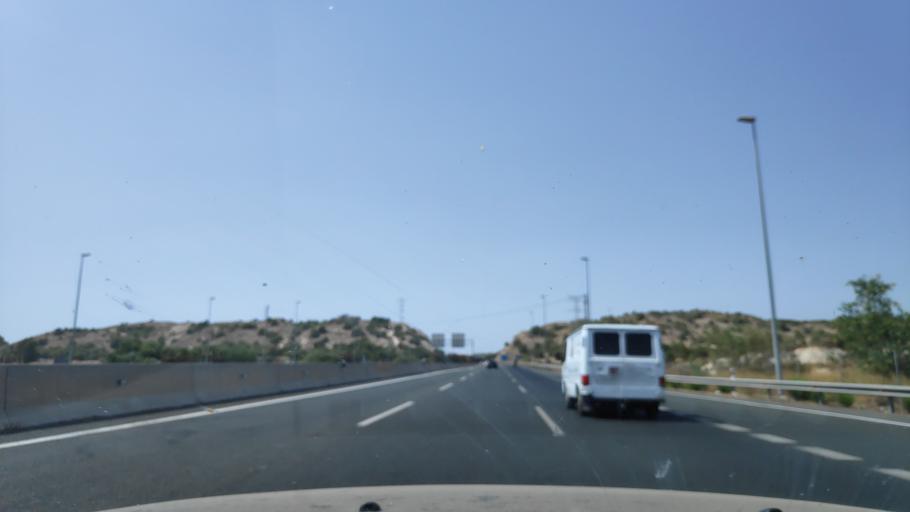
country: ES
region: Murcia
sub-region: Murcia
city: Murcia
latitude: 37.8682
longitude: -1.1232
